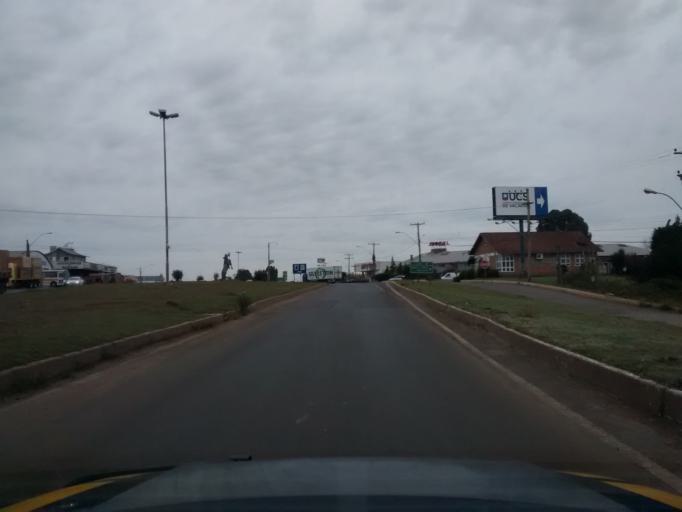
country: BR
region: Rio Grande do Sul
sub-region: Vacaria
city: Vacaria
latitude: -28.5017
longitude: -50.9210
